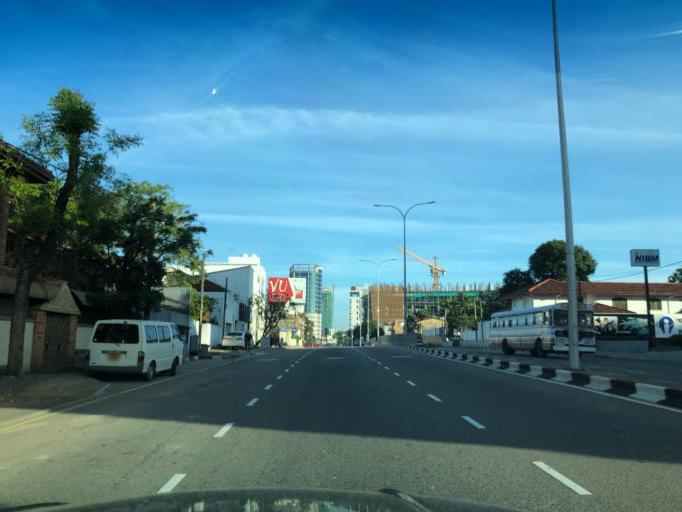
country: LK
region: Western
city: Pita Kotte
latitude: 6.8803
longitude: 79.8763
